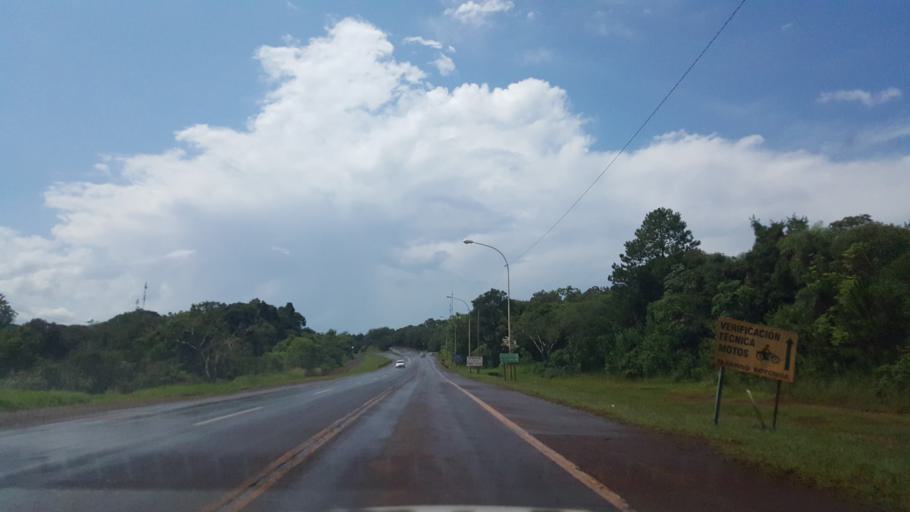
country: AR
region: Misiones
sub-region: Departamento de Eldorado
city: Eldorado
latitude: -26.4087
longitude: -54.6375
